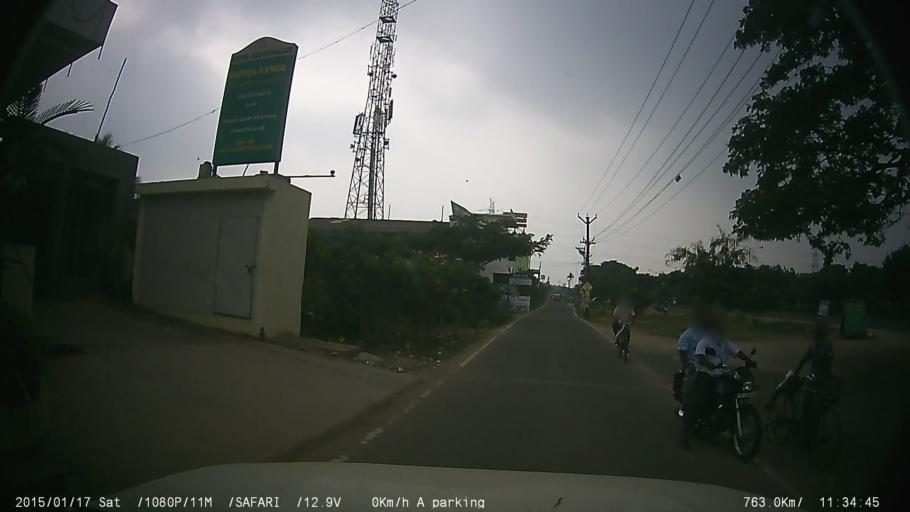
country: IN
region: Tamil Nadu
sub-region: Kancheepuram
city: Madambakkam
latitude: 12.8061
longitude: 80.0277
